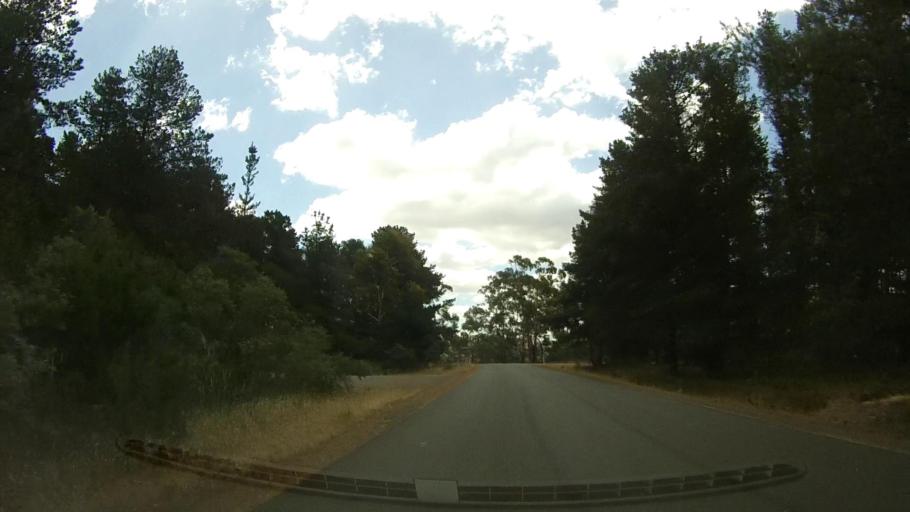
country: AU
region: Tasmania
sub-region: Clarence
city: Seven Mile Beach
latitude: -42.8332
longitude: 147.5221
